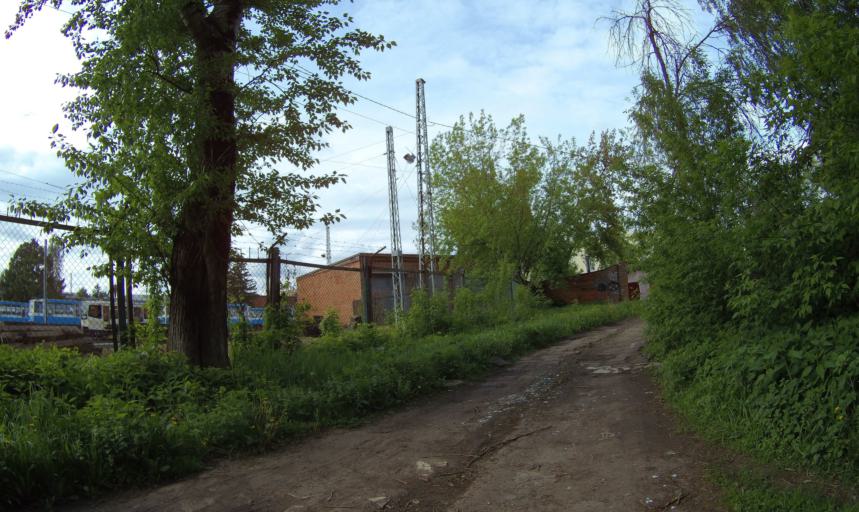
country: RU
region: Moskovskaya
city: Kolomna
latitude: 55.0882
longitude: 38.7691
